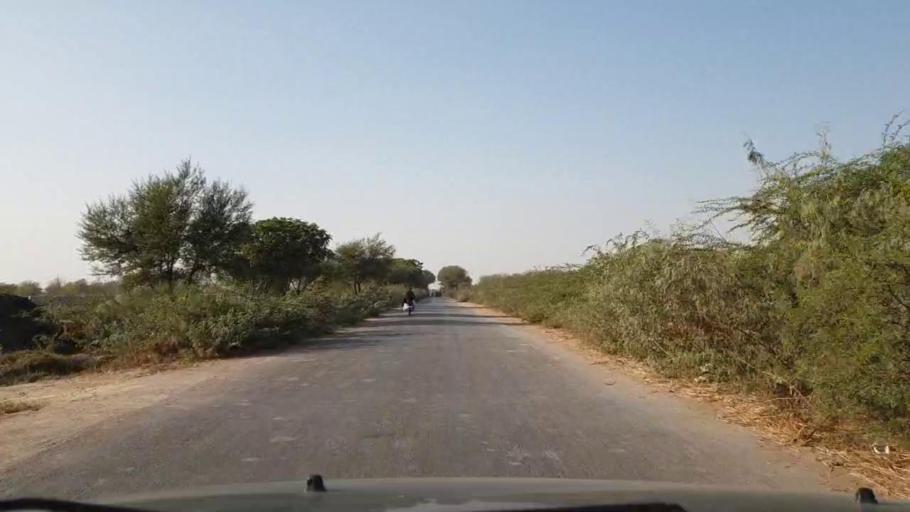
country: PK
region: Sindh
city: Tando Ghulam Ali
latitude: 25.1481
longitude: 68.8631
